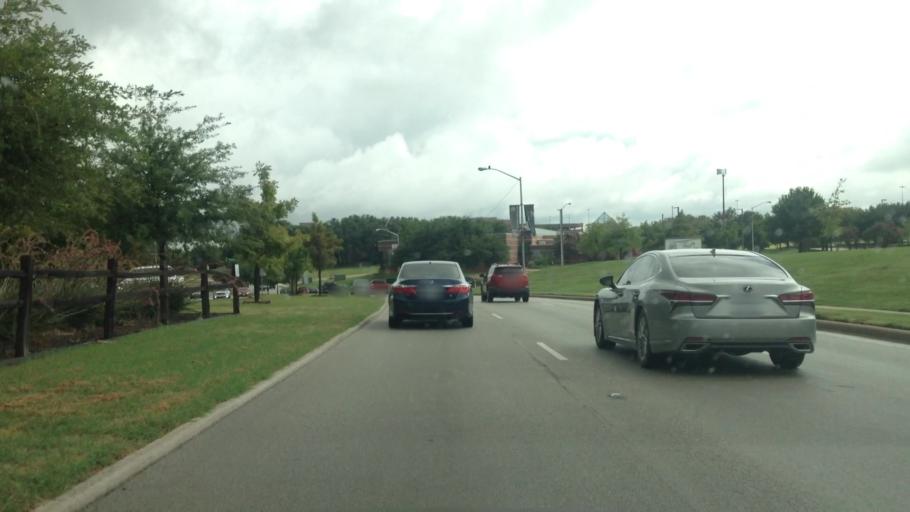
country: US
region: Texas
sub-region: Tarrant County
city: Edgecliff Village
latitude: 32.6909
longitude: -97.3940
